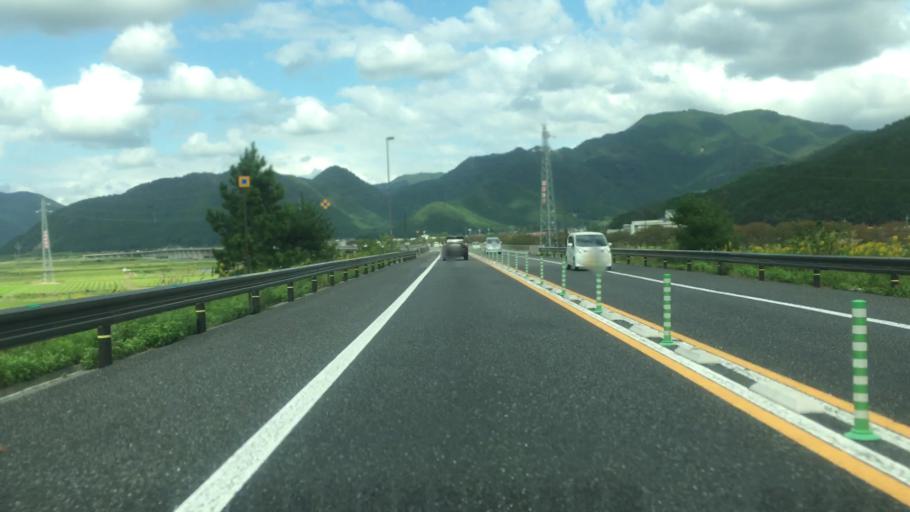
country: JP
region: Kyoto
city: Fukuchiyama
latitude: 35.1909
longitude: 135.0416
